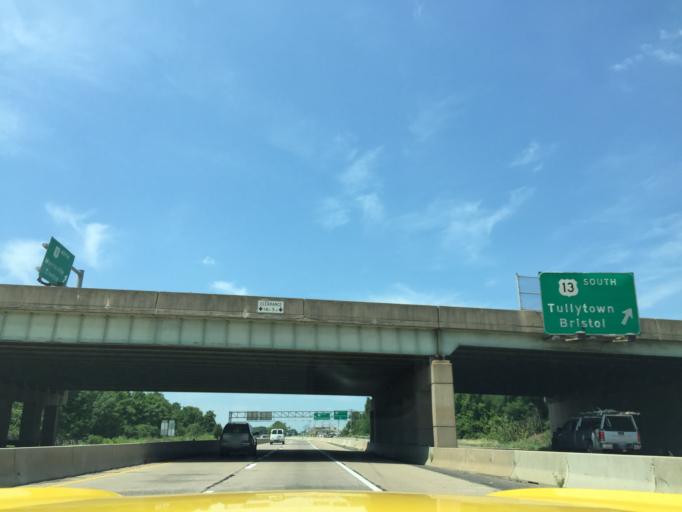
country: US
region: Pennsylvania
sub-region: Bucks County
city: Morrisville
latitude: 40.1969
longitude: -74.8017
